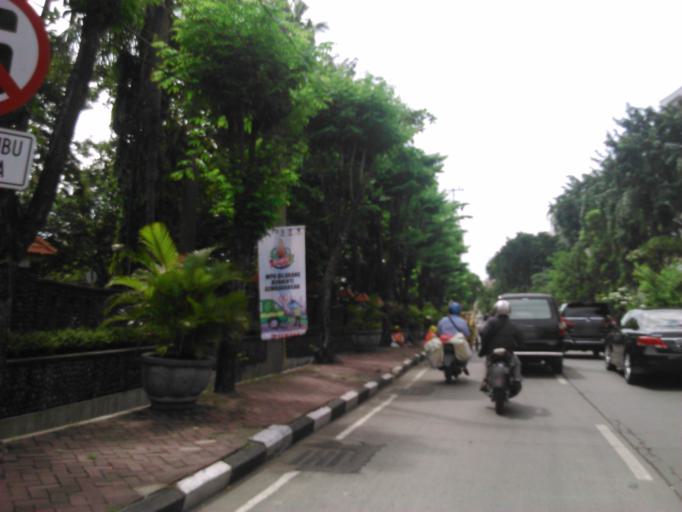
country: ID
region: East Java
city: Jagirsidosermo
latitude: -7.2912
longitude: 112.7160
